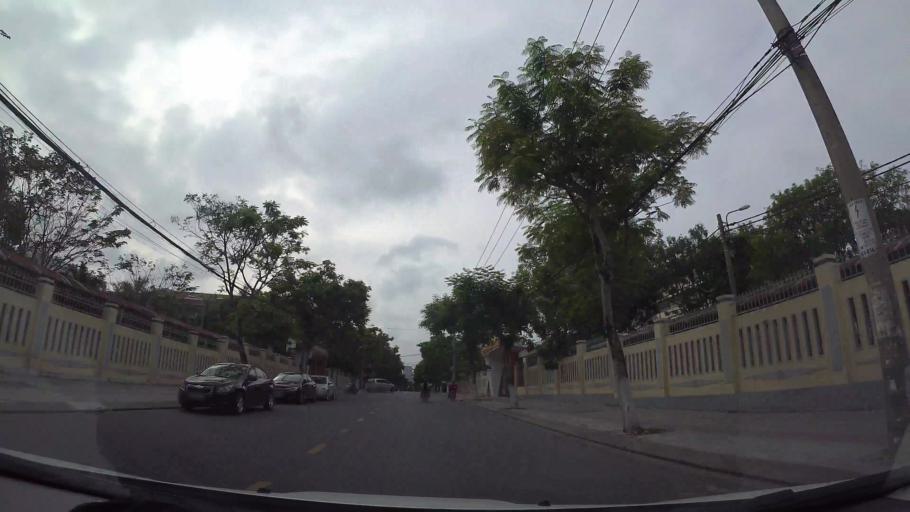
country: VN
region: Da Nang
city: Son Tra
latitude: 16.0661
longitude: 108.2378
